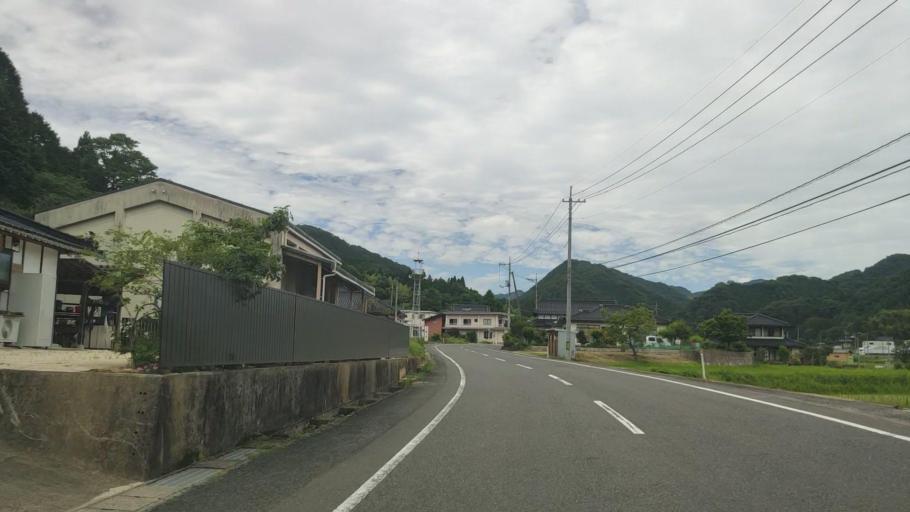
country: JP
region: Hyogo
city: Yamazakicho-nakabirose
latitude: 35.0976
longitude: 134.2967
